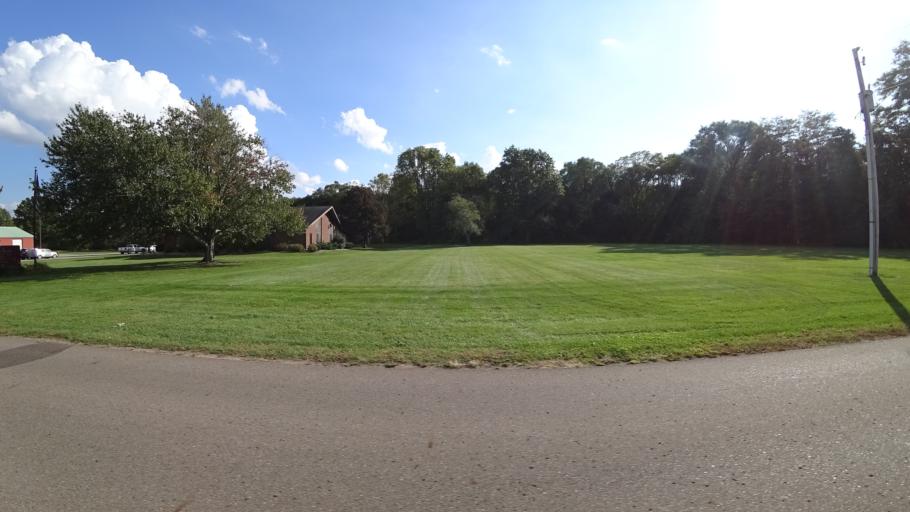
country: US
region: Michigan
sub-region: Saint Joseph County
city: Three Rivers
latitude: 41.9475
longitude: -85.6135
